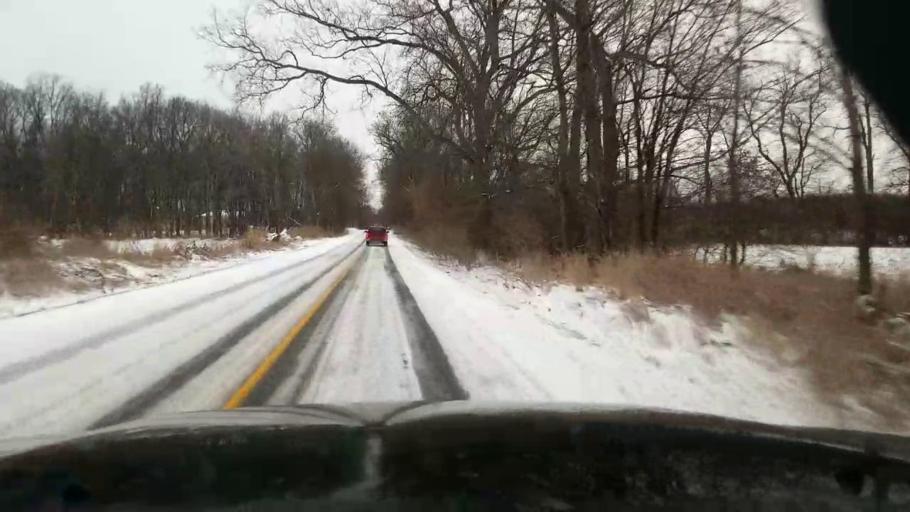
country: US
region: Michigan
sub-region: Jackson County
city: Spring Arbor
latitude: 42.1411
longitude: -84.4989
